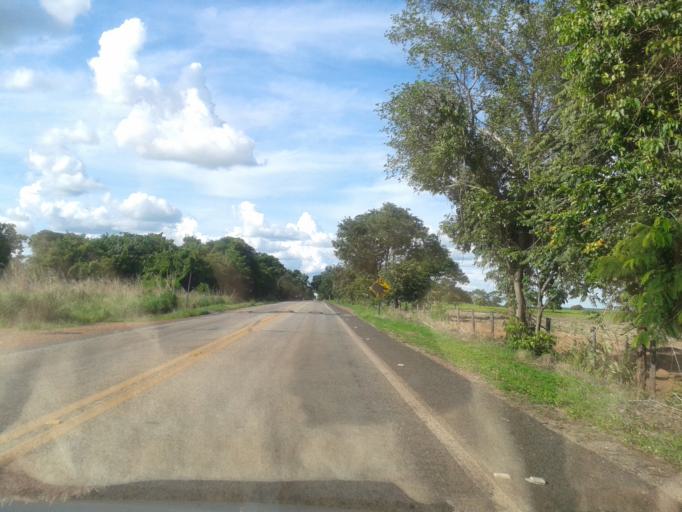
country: BR
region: Goias
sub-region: Mozarlandia
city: Mozarlandia
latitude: -14.6388
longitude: -50.5196
